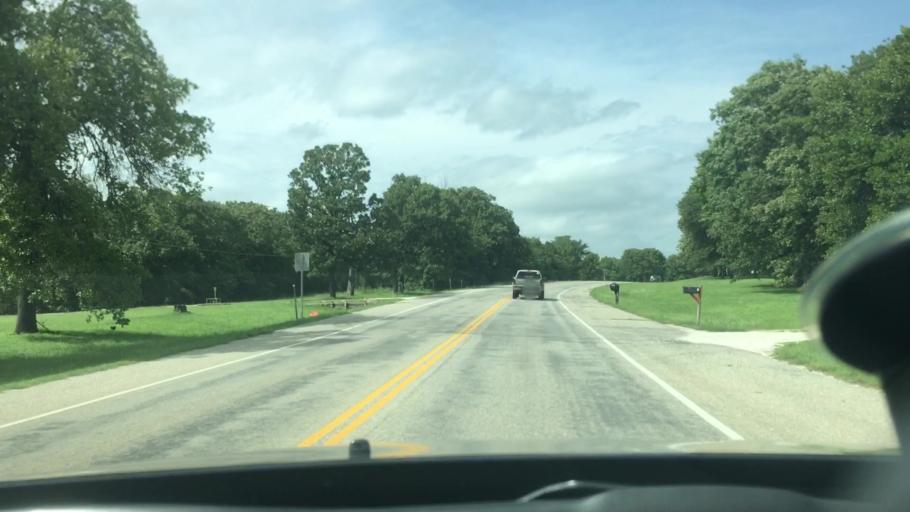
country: US
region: Oklahoma
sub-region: Pontotoc County
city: Byng
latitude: 34.8497
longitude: -96.6786
